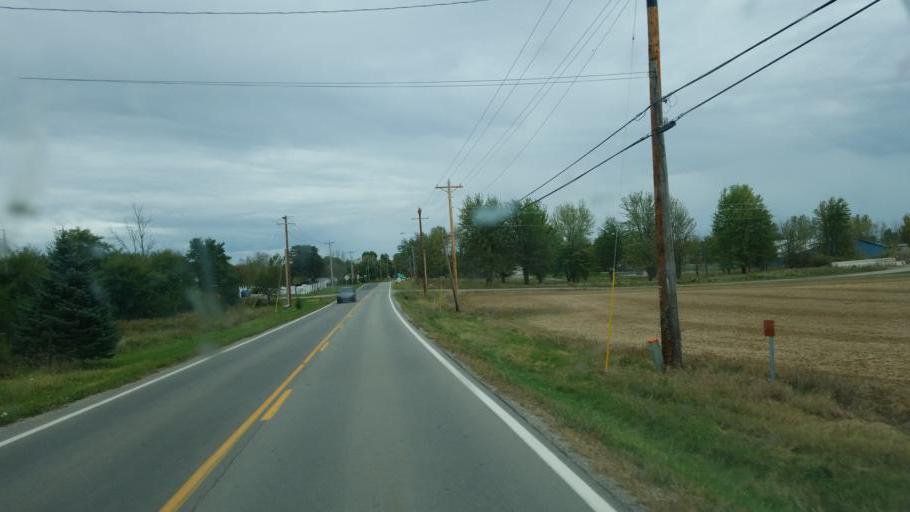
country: US
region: Ohio
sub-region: Huron County
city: New London
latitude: 41.0960
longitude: -82.4023
